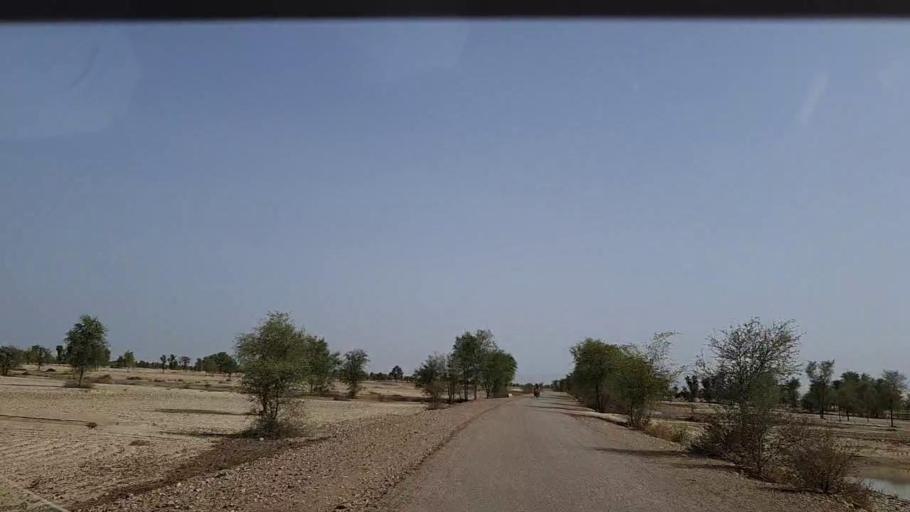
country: PK
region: Sindh
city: Johi
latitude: 26.6264
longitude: 67.5008
